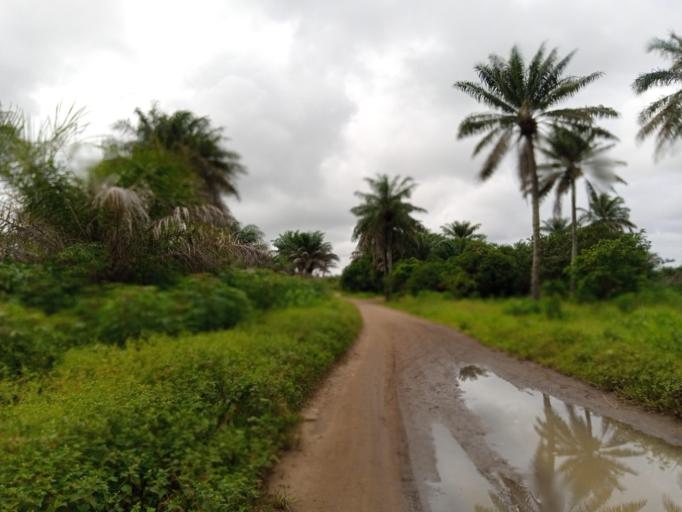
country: SL
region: Northern Province
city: Masoyila
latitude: 8.5842
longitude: -13.1934
